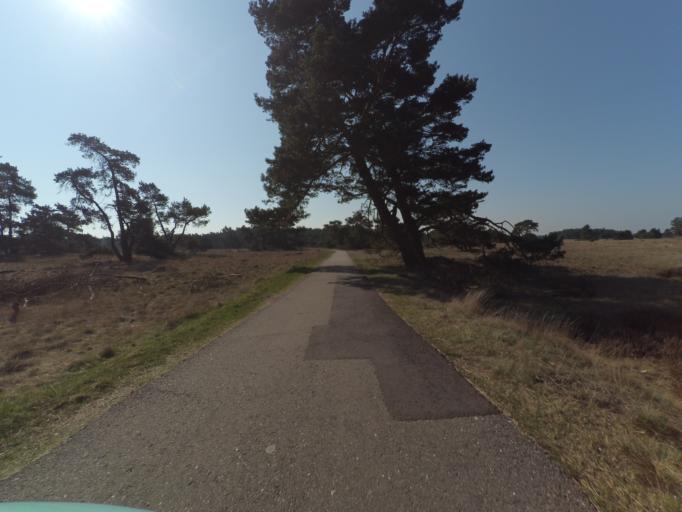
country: NL
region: Gelderland
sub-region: Gemeente Ede
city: Otterlo
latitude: 52.0712
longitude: 5.8256
